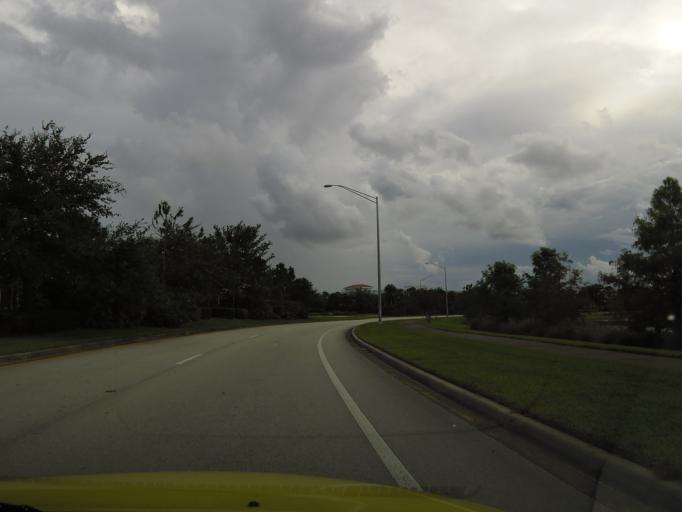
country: US
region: Florida
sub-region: Palm Beach County
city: North Palm Beach
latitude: 26.8430
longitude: -80.0920
